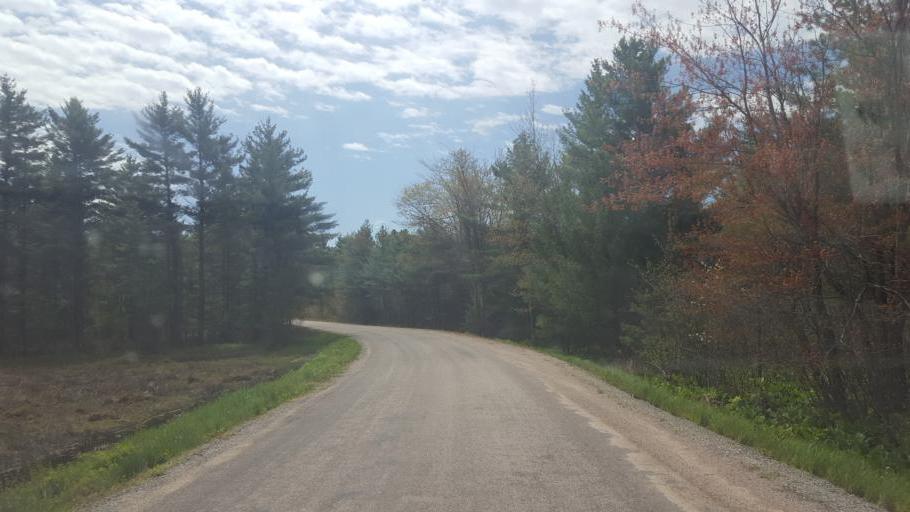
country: US
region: Wisconsin
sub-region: Clark County
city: Neillsville
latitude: 44.3145
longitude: -90.5106
